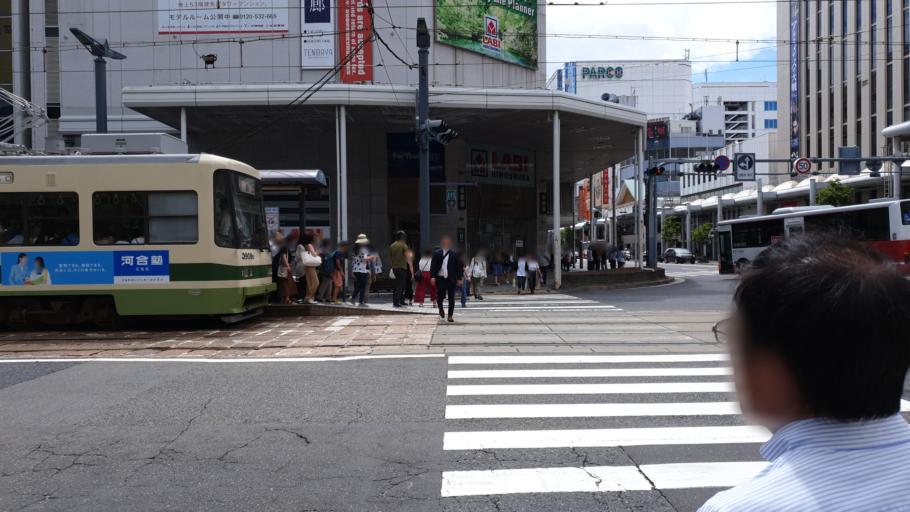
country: JP
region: Hiroshima
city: Hiroshima-shi
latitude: 34.3939
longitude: 132.4638
